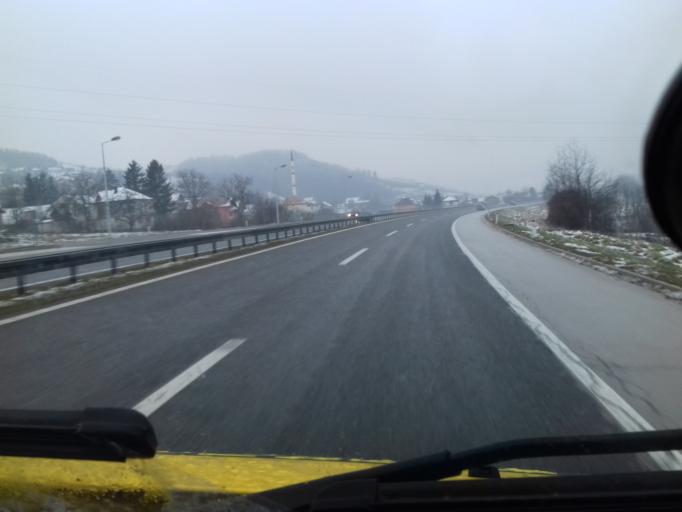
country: BA
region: Federation of Bosnia and Herzegovina
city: Visoko
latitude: 43.9912
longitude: 18.2047
